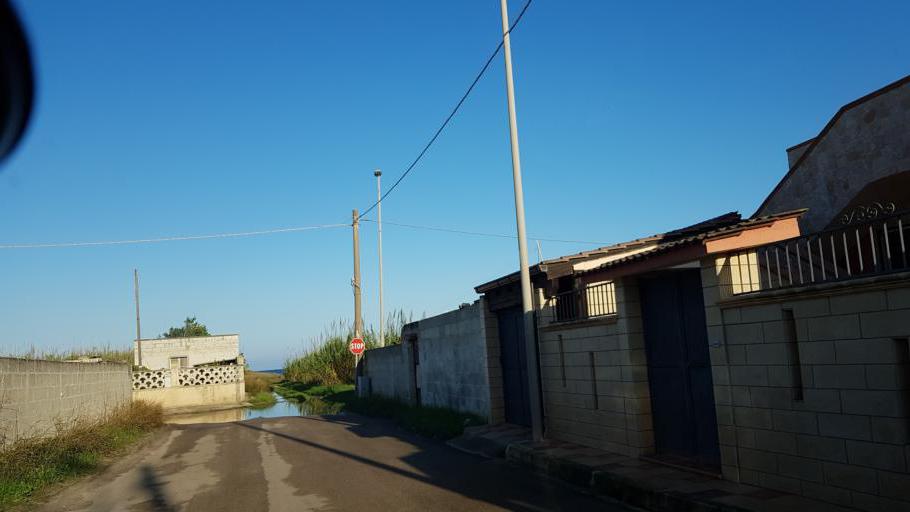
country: IT
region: Apulia
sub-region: Provincia di Brindisi
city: Torchiarolo
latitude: 40.5146
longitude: 18.0963
